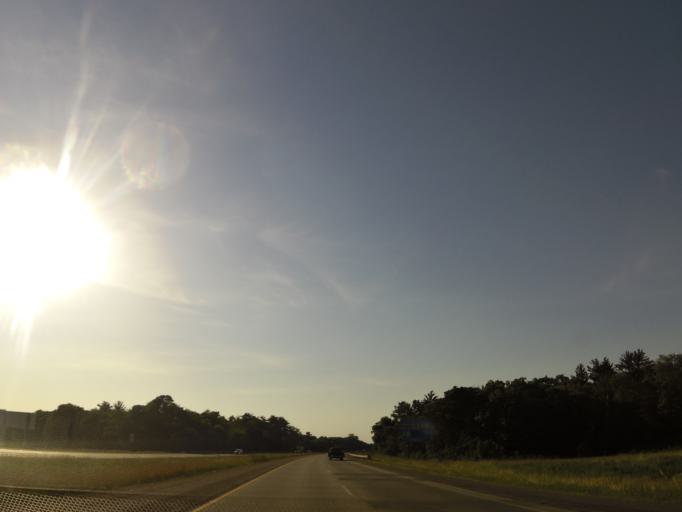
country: US
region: Wisconsin
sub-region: Juneau County
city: Mauston
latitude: 43.7859
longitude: -90.0458
